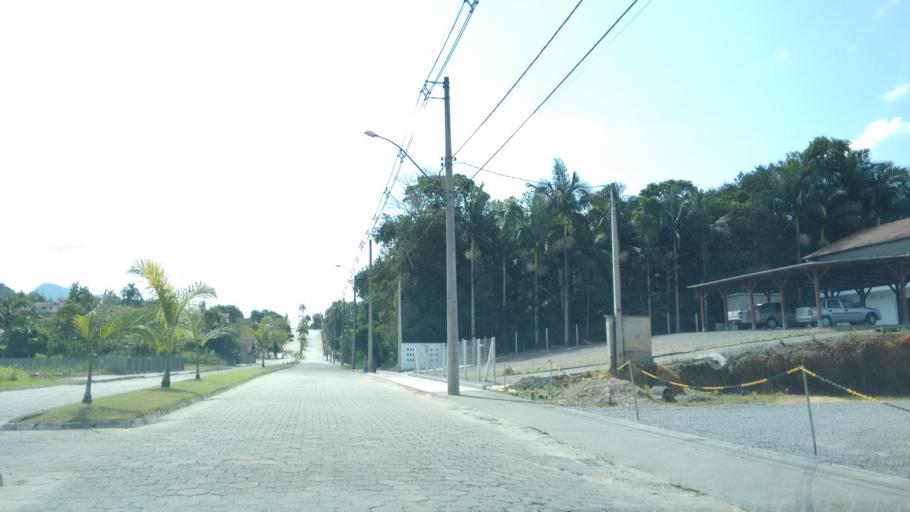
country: BR
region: Santa Catarina
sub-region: Pomerode
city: Pomerode
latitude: -26.7524
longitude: -49.1749
